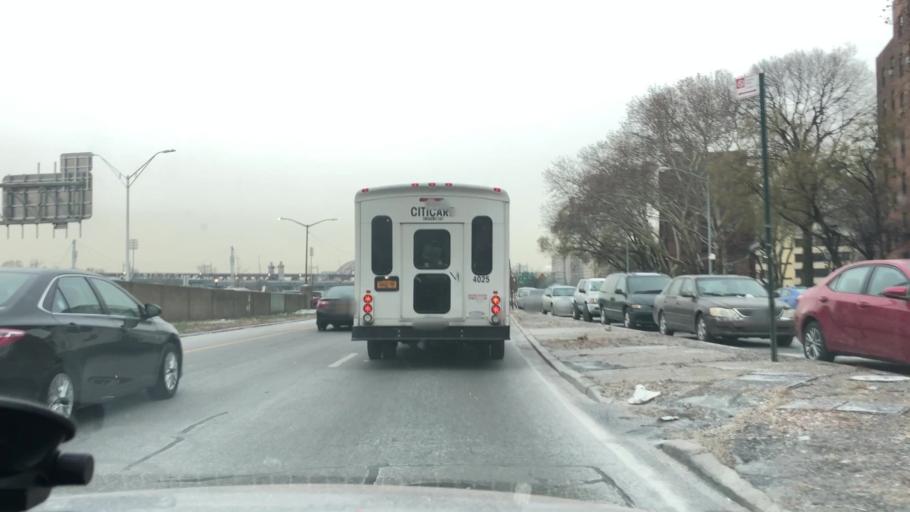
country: US
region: New York
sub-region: New York County
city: Manhattan
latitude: 40.7988
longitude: -73.9296
